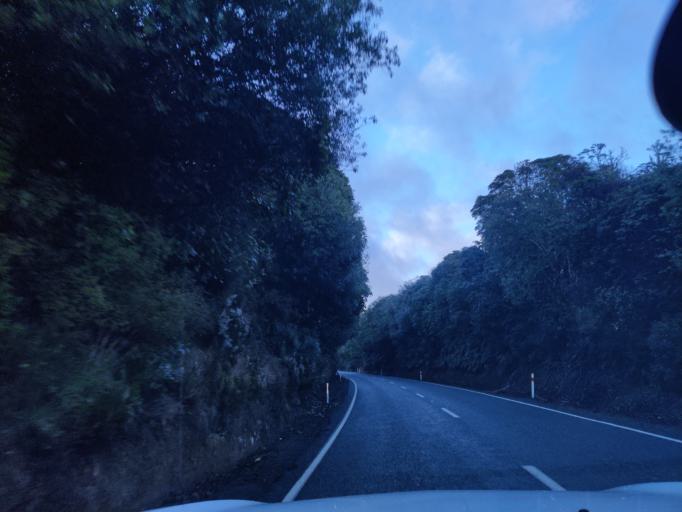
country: NZ
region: Waikato
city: Turangi
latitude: -38.7133
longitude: 175.6641
